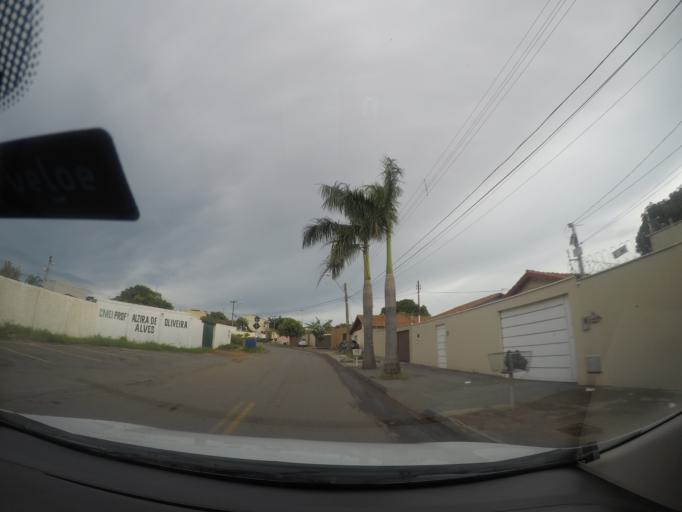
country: BR
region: Goias
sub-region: Goiania
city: Goiania
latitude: -16.7300
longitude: -49.3090
